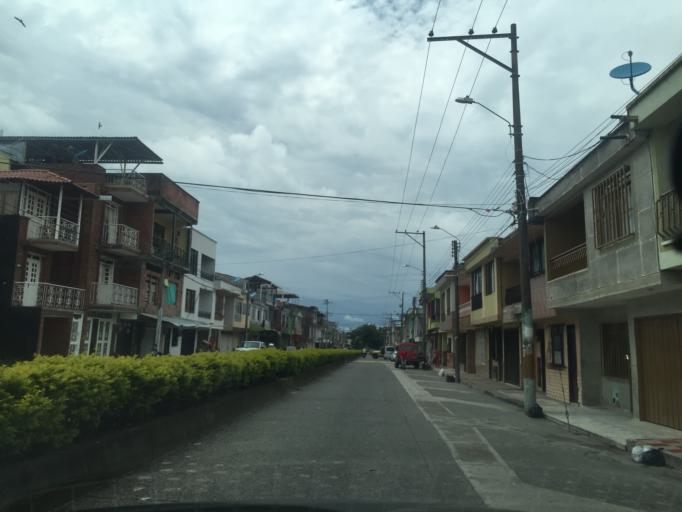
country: CO
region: Quindio
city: Montenegro
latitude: 4.5622
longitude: -75.7478
